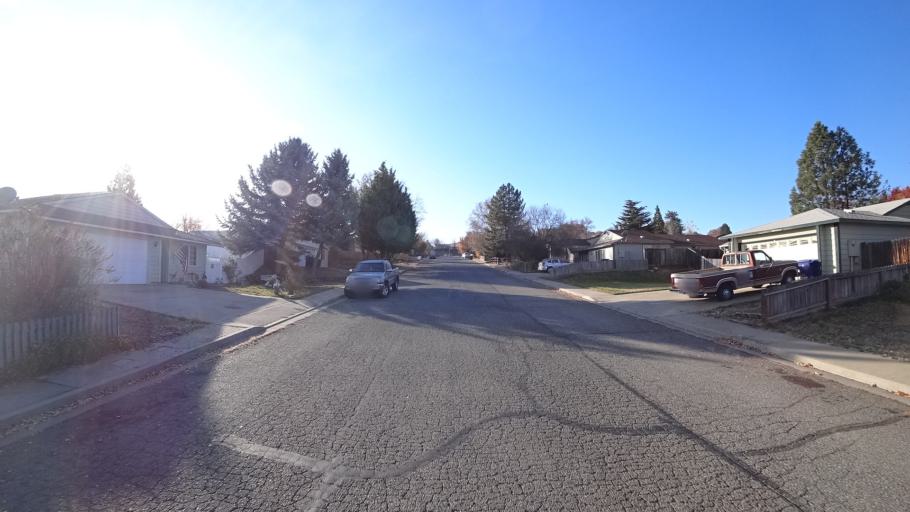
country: US
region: California
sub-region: Siskiyou County
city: Yreka
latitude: 41.7117
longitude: -122.6233
